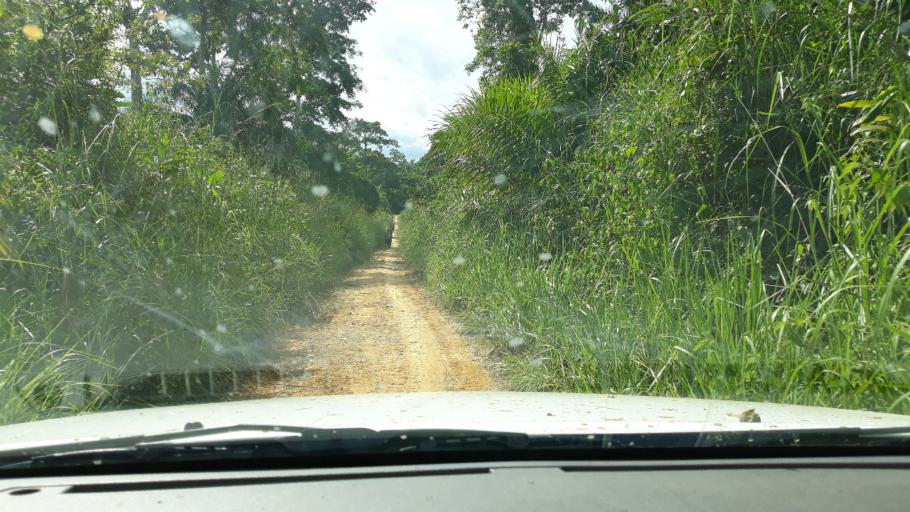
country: CD
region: Maniema
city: Kampene
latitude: -2.7549
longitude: 26.9265
